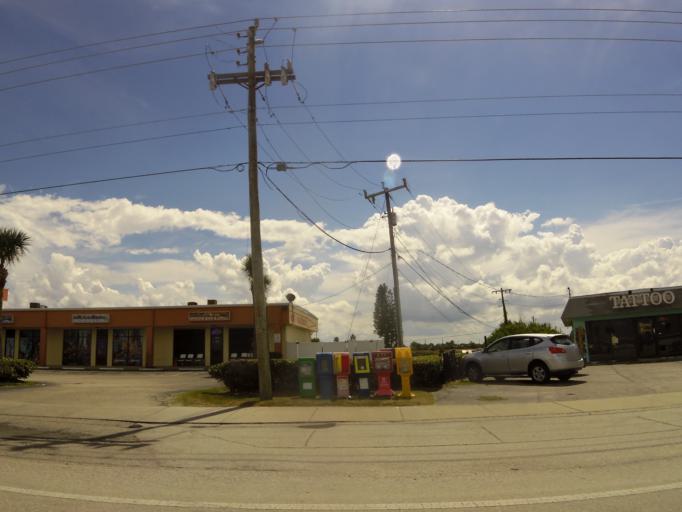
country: US
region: Florida
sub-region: Volusia County
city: Ormond-by-the-Sea
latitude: 29.3291
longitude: -81.0582
